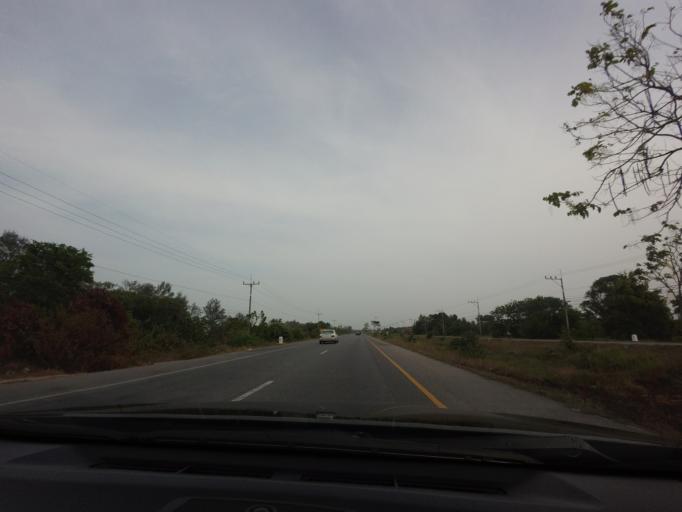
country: TH
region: Songkhla
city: Thepha
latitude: 6.9203
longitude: 100.8934
